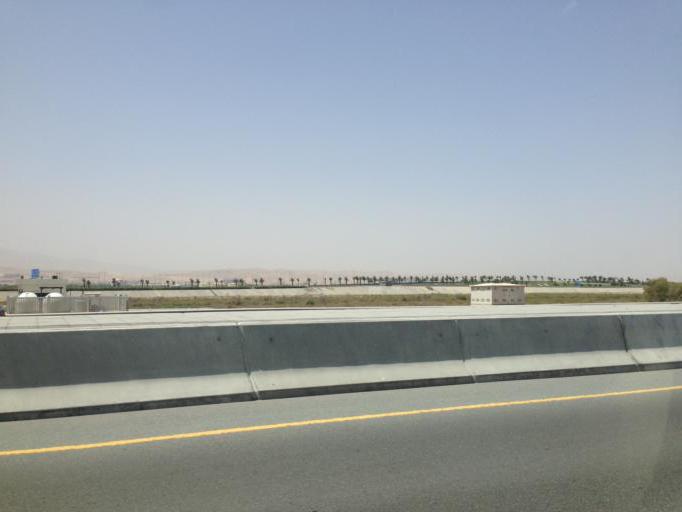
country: OM
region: Muhafazat Masqat
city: Bawshar
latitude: 23.6067
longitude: 58.3192
